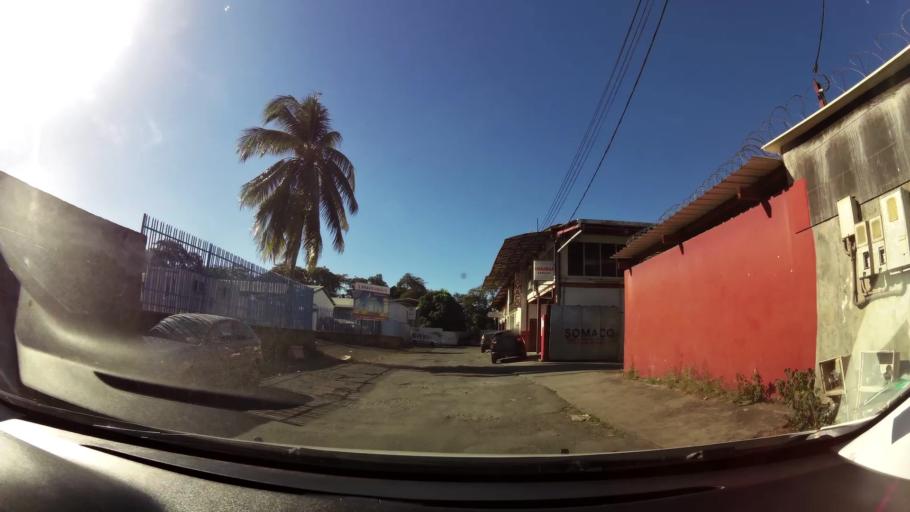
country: YT
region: Mamoudzou
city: Mamoudzou
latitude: -12.7680
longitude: 45.2261
